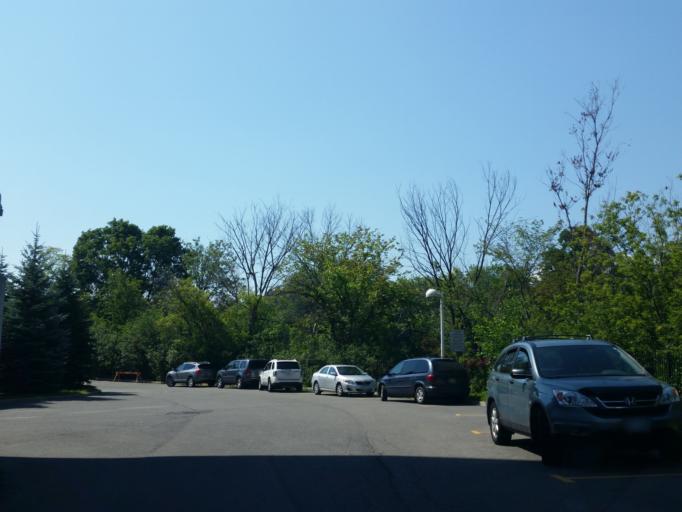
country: CA
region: Ontario
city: Ottawa
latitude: 45.4381
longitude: -75.6830
